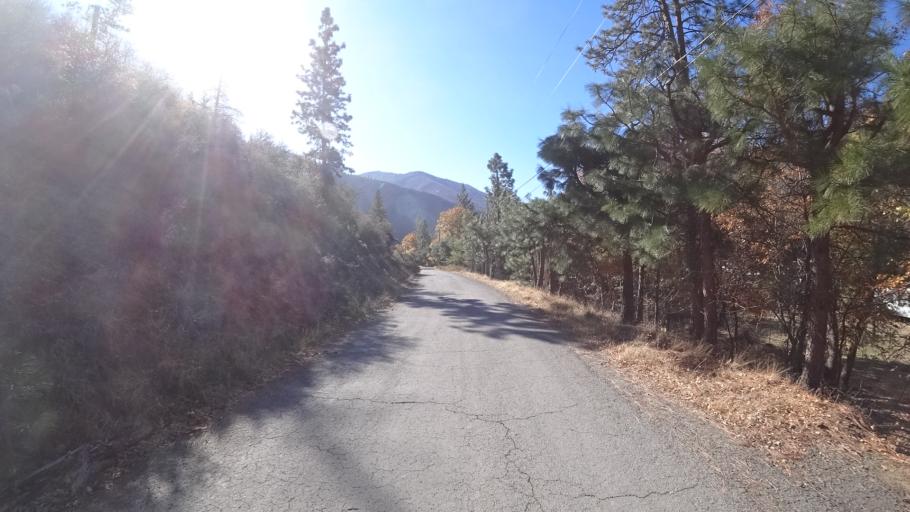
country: US
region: California
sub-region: Siskiyou County
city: Yreka
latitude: 41.8332
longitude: -122.6380
